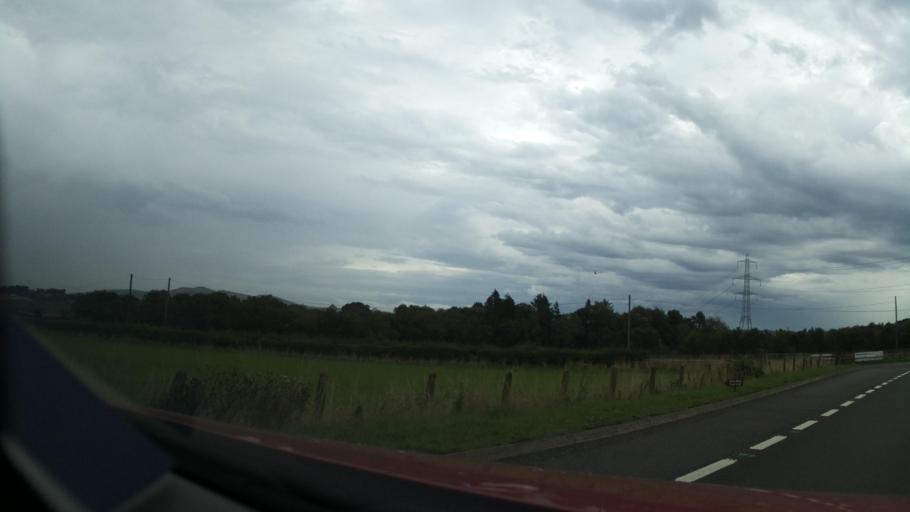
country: GB
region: Scotland
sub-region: Fife
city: High Valleyfield
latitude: 56.0665
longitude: -3.6245
